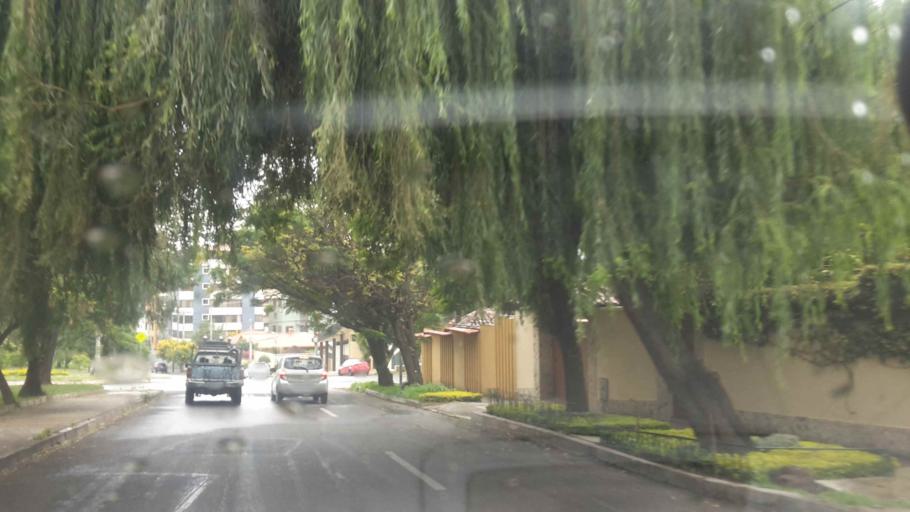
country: BO
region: Cochabamba
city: Cochabamba
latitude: -17.3680
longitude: -66.1582
